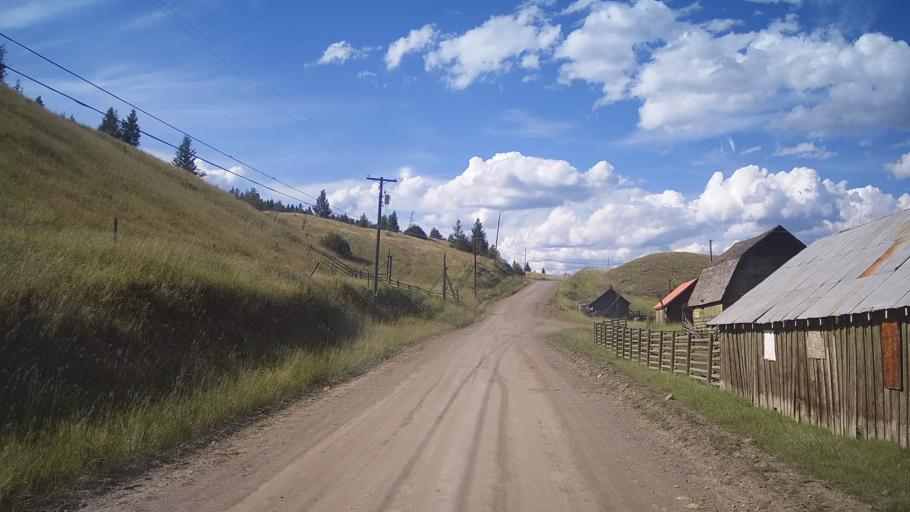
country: CA
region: British Columbia
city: Lillooet
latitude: 51.3046
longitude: -121.9867
